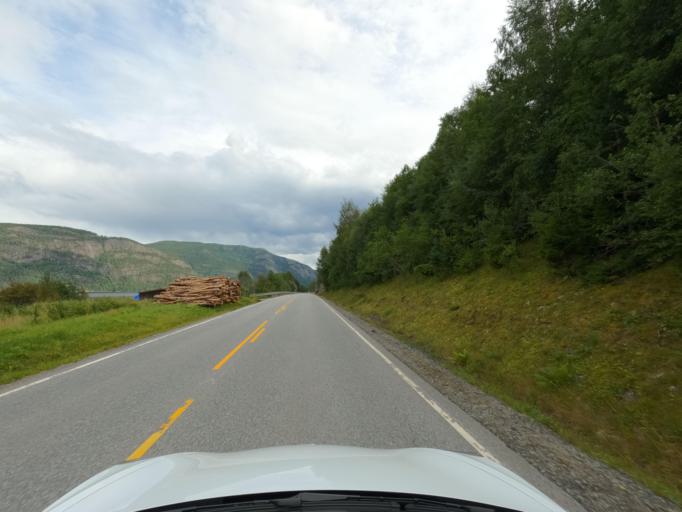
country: NO
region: Telemark
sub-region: Tinn
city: Rjukan
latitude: 59.9181
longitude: 8.8692
